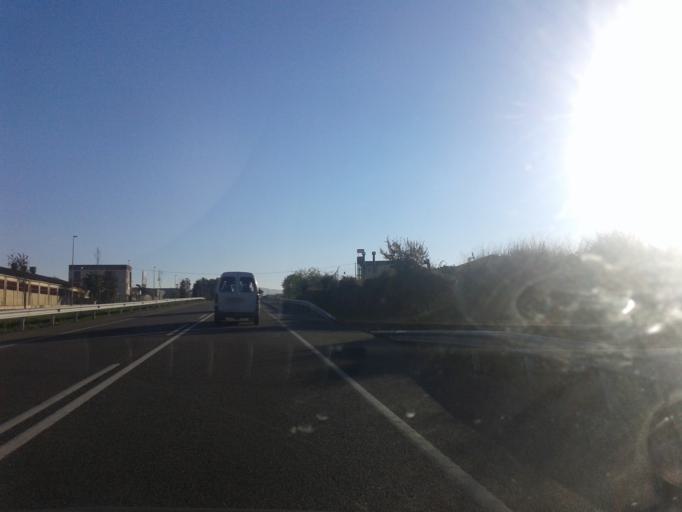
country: ES
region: Catalonia
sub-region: Provincia de Barcelona
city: Avinyonet del Penedes
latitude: 41.3601
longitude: 1.7644
